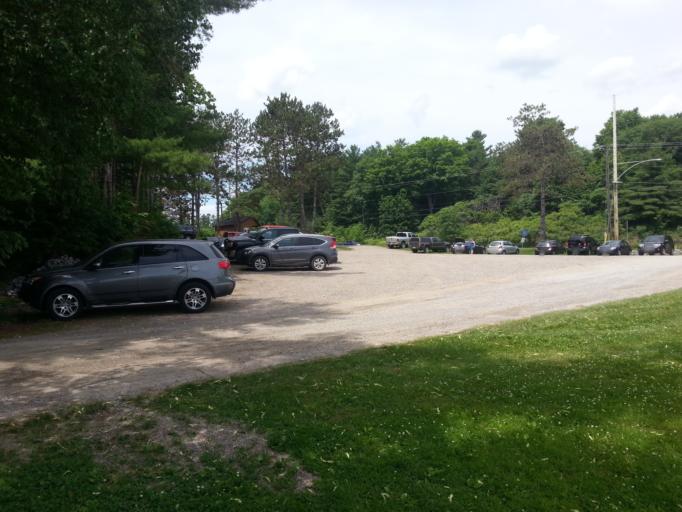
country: CA
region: Ontario
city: Renfrew
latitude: 45.2933
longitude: -76.7400
